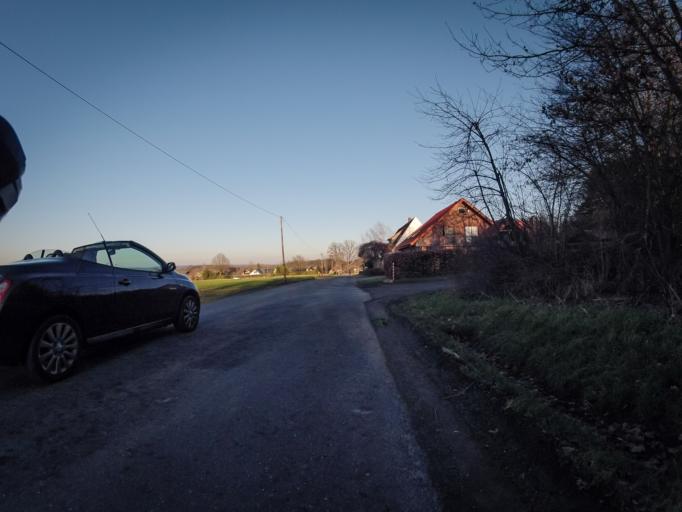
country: DE
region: Lower Saxony
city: Wallenhorst
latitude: 52.3266
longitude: 8.0168
